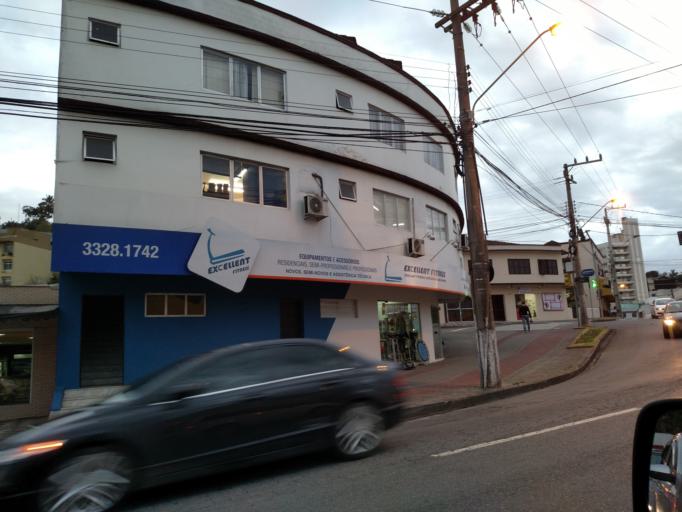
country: BR
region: Santa Catarina
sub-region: Blumenau
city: Blumenau
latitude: -26.9144
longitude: -49.0747
